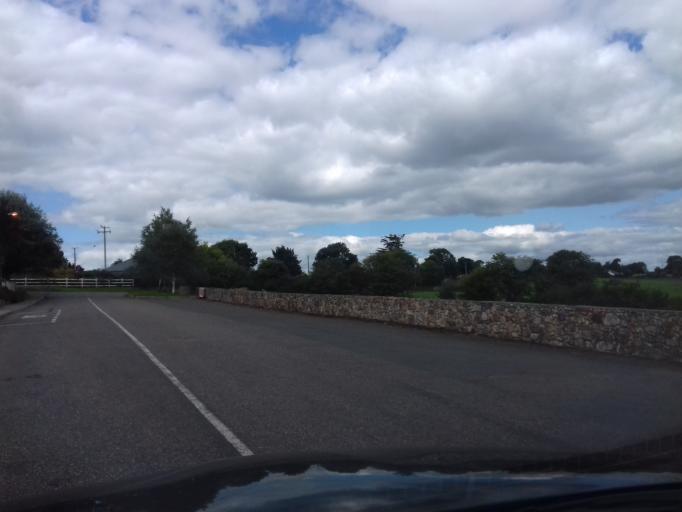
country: IE
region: Munster
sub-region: Waterford
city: Tra Mhor
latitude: 52.1733
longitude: -7.2626
